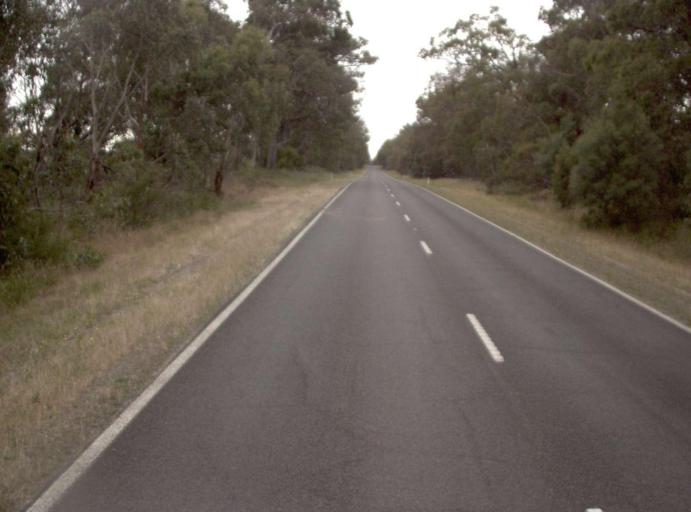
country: AU
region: Victoria
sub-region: Latrobe
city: Traralgon
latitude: -38.5417
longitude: 146.8388
